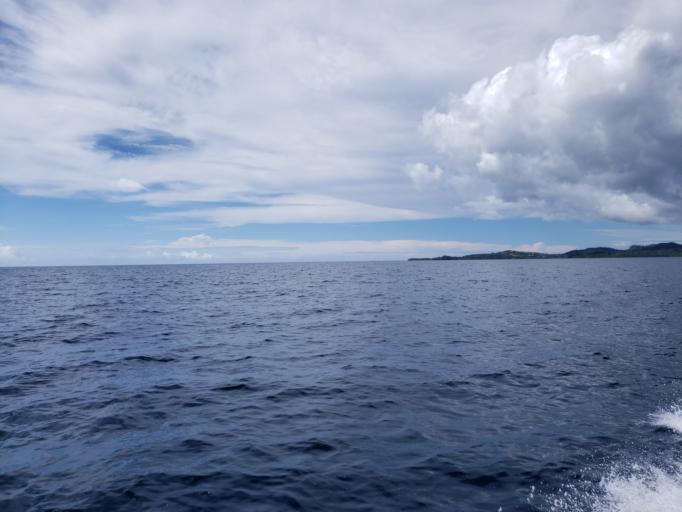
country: PW
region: Koror
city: Koror Town
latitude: 7.3935
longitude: 134.4700
